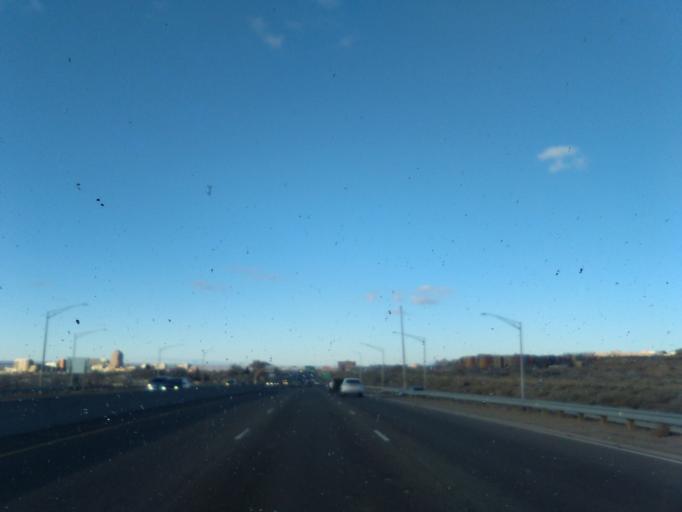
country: US
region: New Mexico
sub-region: Bernalillo County
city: Albuquerque
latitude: 35.0606
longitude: -106.6383
